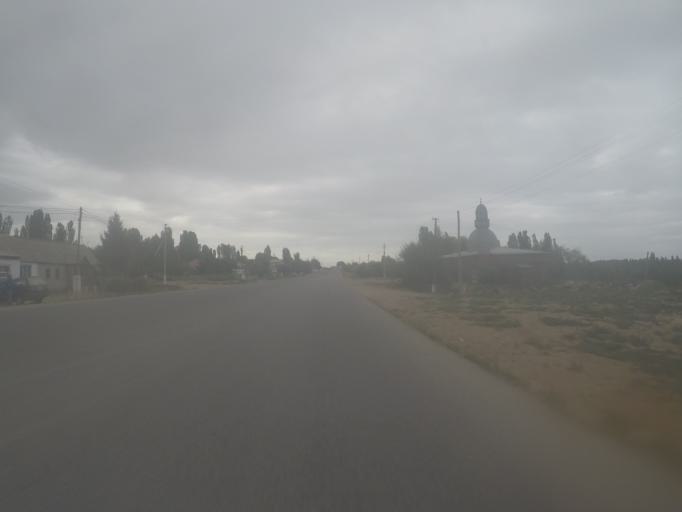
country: KG
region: Ysyk-Koel
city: Cholpon-Ata
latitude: 42.6910
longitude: 77.3576
